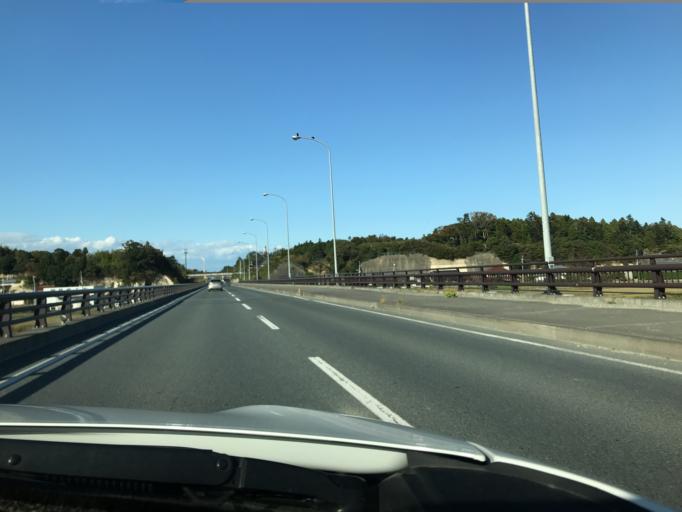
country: JP
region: Miyagi
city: Marumori
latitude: 37.8058
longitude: 140.9436
